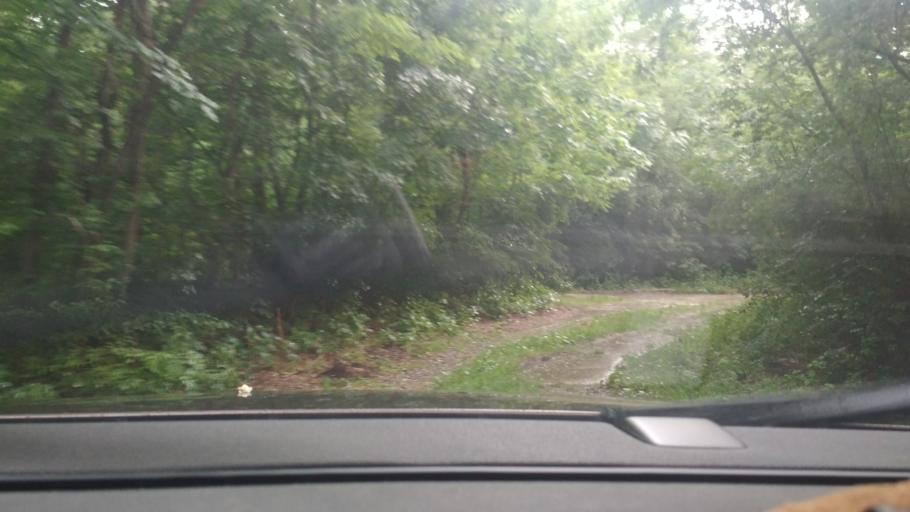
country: MD
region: Singerei
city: Biruinta
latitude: 47.7513
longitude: 28.1477
